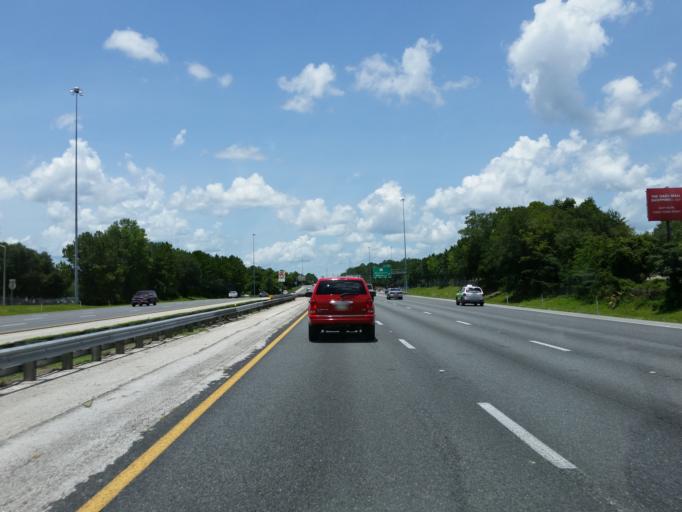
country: US
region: Florida
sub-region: Alachua County
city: Gainesville
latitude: 29.6542
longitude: -82.4142
